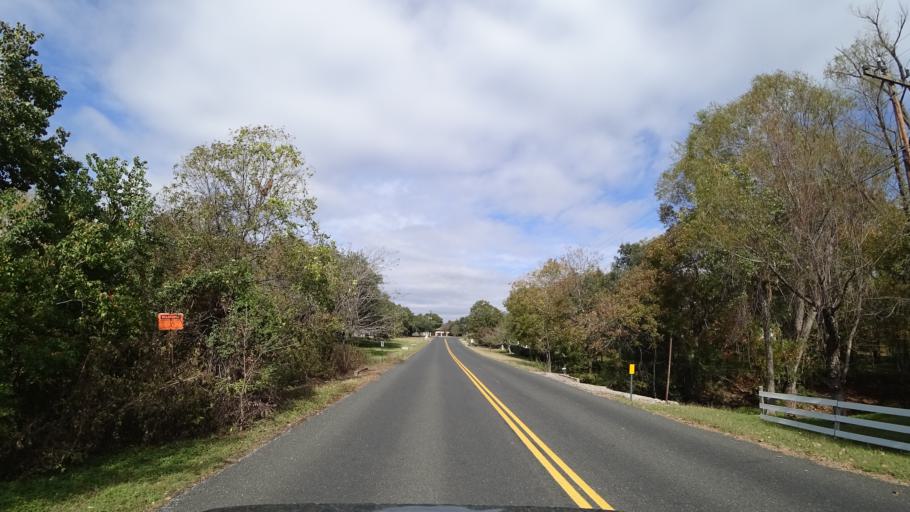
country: US
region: Texas
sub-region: Williamson County
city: Brushy Creek
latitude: 30.5317
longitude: -97.7385
